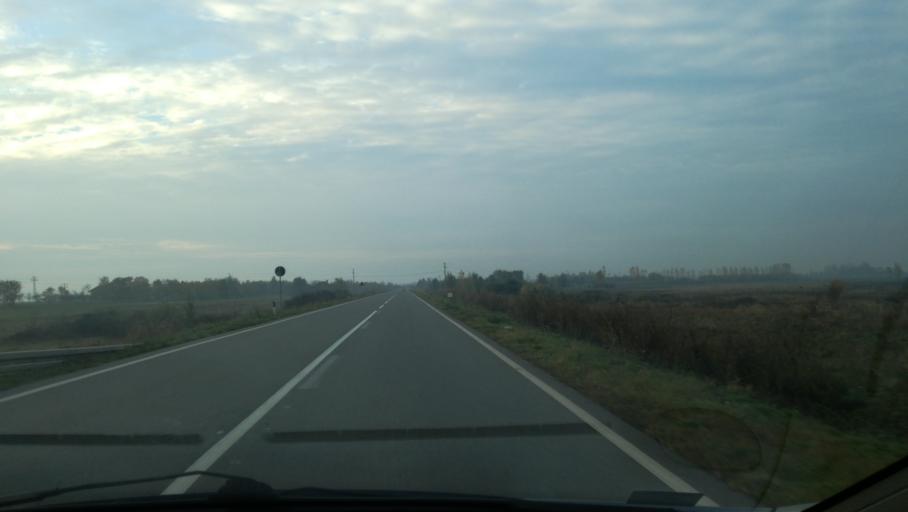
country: RS
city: Banatska Topola
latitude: 45.6923
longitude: 20.4222
